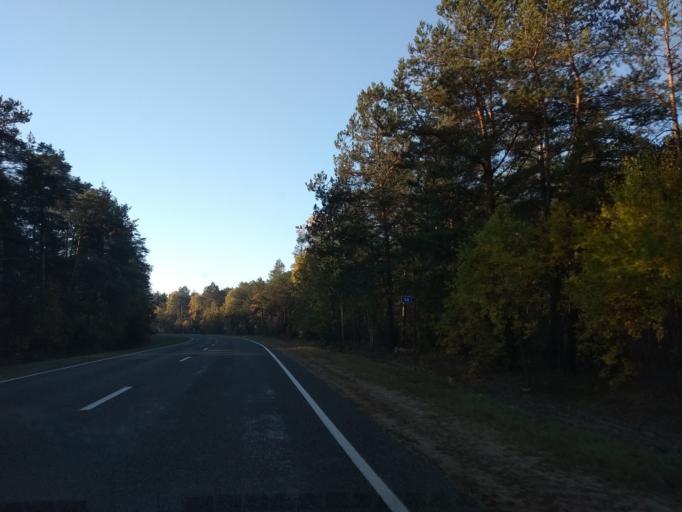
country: BY
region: Brest
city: Kobryn
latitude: 52.0995
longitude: 24.2785
